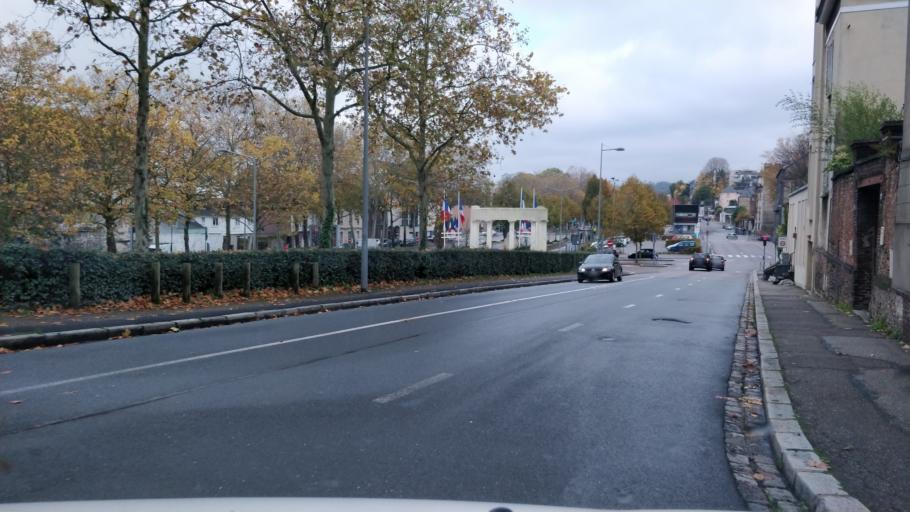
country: FR
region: Haute-Normandie
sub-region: Departement de la Seine-Maritime
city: Rouen
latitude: 49.4461
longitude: 1.1084
